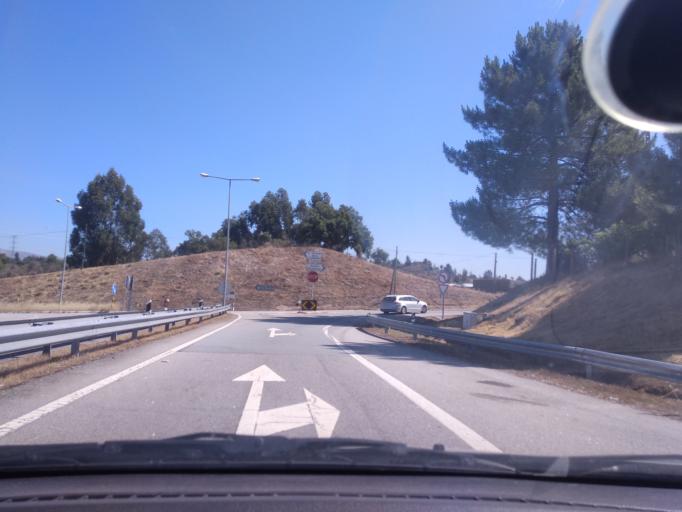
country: PT
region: Guarda
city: Alcains
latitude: 39.9177
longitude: -7.4759
